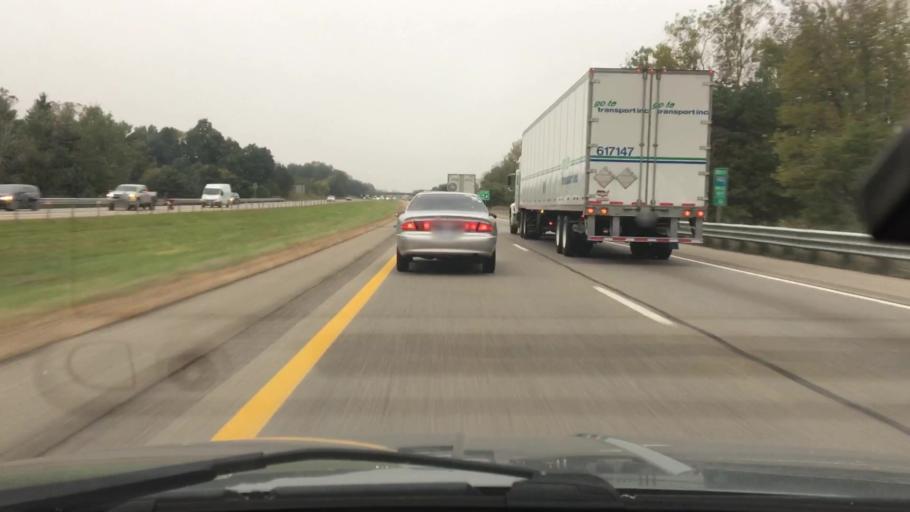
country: US
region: Michigan
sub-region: Calhoun County
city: Lakeview
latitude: 42.2653
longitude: -85.2268
